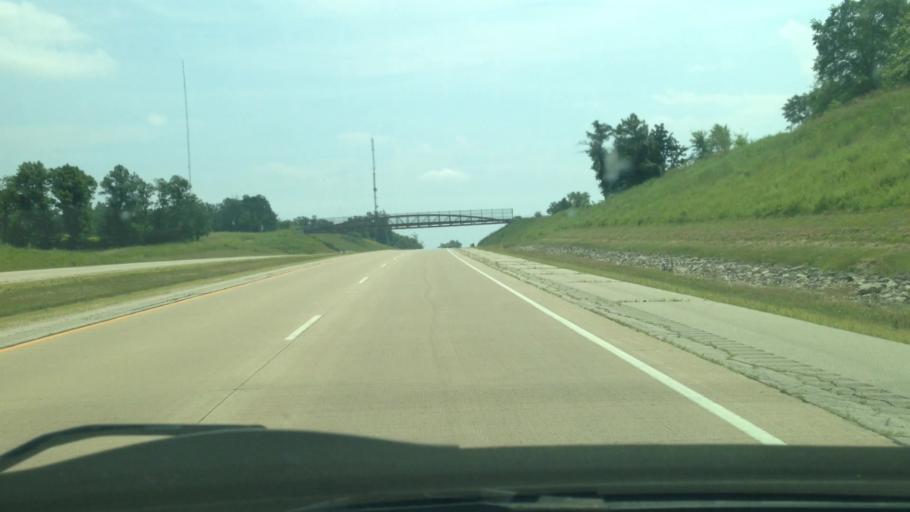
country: US
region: Wisconsin
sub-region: Dane County
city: Cross Plains
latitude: 43.2144
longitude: -89.6084
